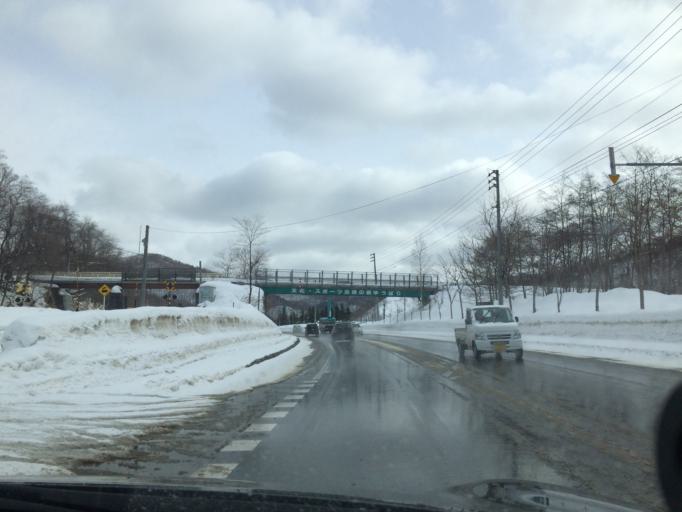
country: JP
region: Hokkaido
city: Iwamizawa
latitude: 43.0201
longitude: 141.9795
